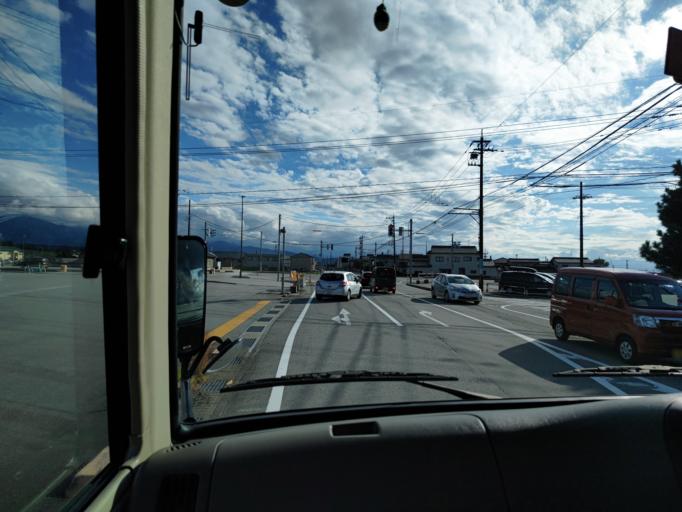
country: JP
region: Toyama
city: Nyuzen
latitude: 36.8812
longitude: 137.4466
